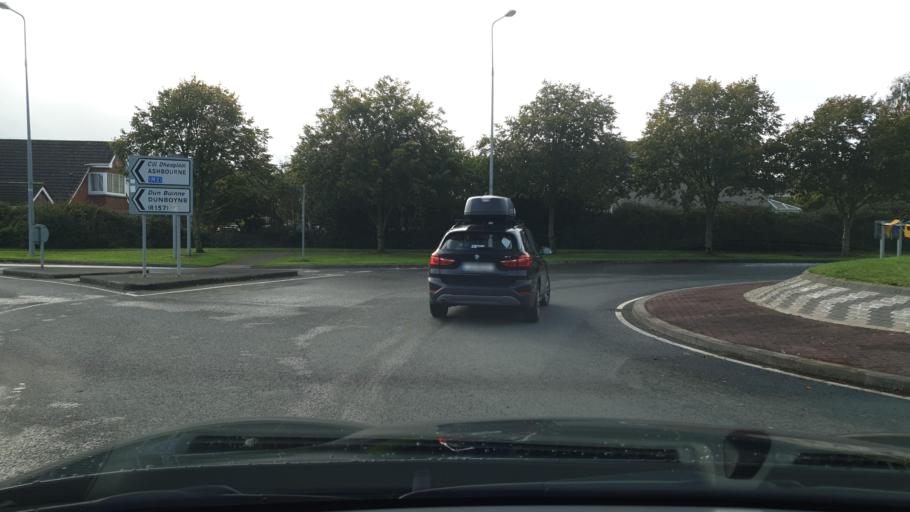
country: IE
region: Leinster
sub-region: An Mhi
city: Ratoath
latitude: 53.5086
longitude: -6.4708
